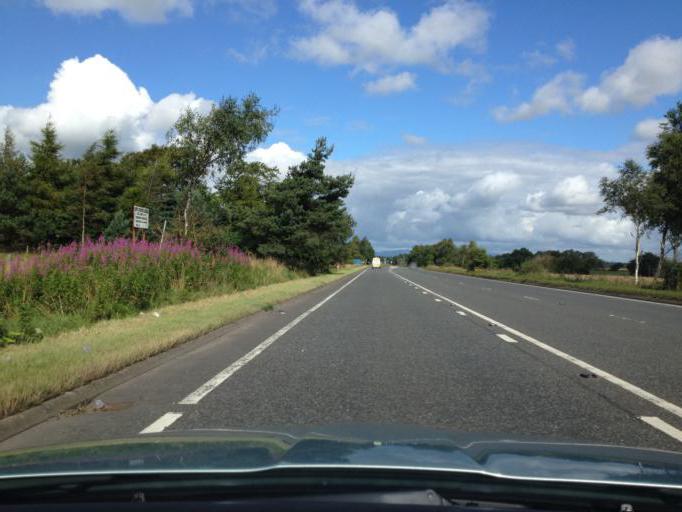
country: GB
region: Scotland
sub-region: West Lothian
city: Bathgate
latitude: 55.9135
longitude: -3.6759
